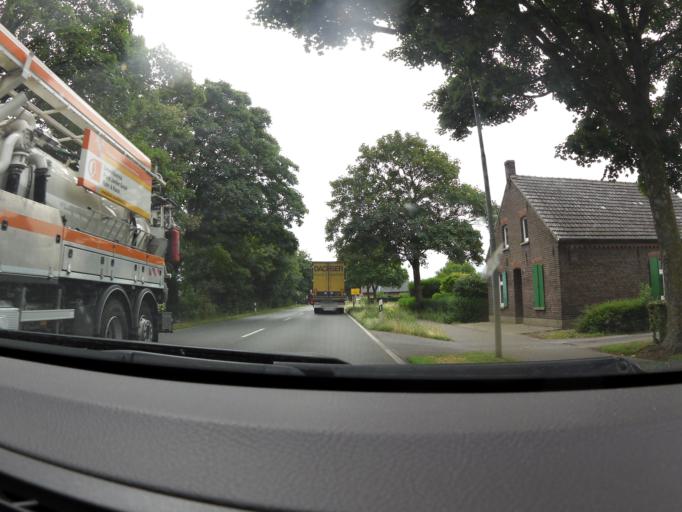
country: DE
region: North Rhine-Westphalia
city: Straelen
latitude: 51.4660
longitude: 6.2819
